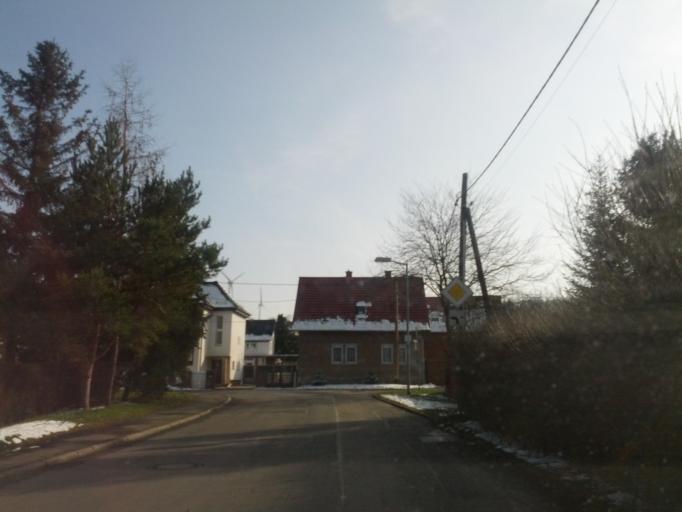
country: DE
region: Thuringia
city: Ichtershausen
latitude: 50.9202
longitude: 10.9869
